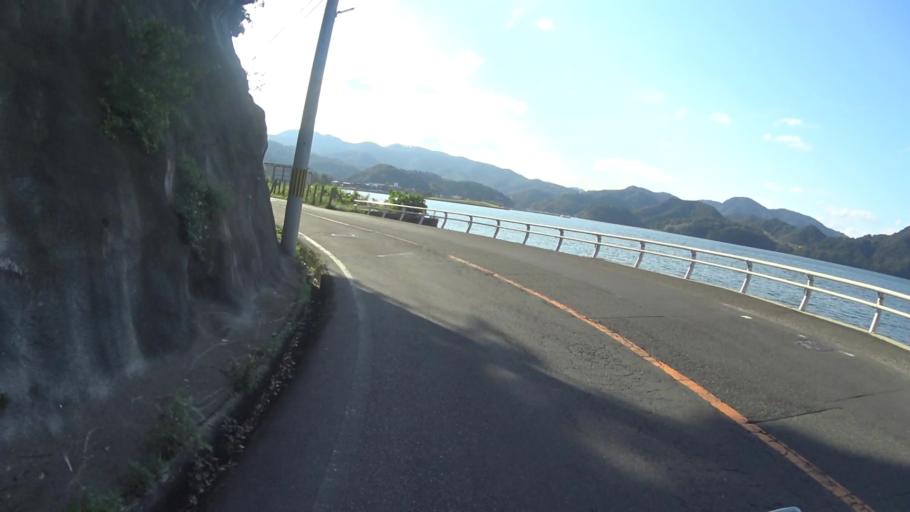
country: JP
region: Hyogo
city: Toyooka
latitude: 35.6066
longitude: 134.9058
